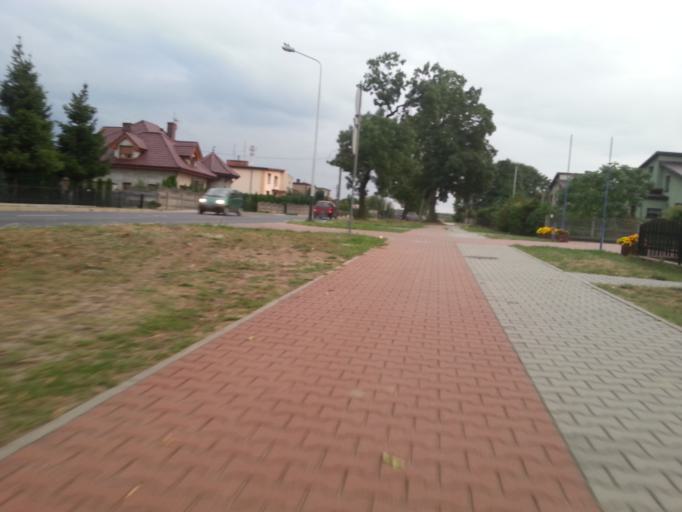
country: PL
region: Lower Silesian Voivodeship
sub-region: Powiat olesnicki
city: Twardogora
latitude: 51.3629
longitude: 17.4579
